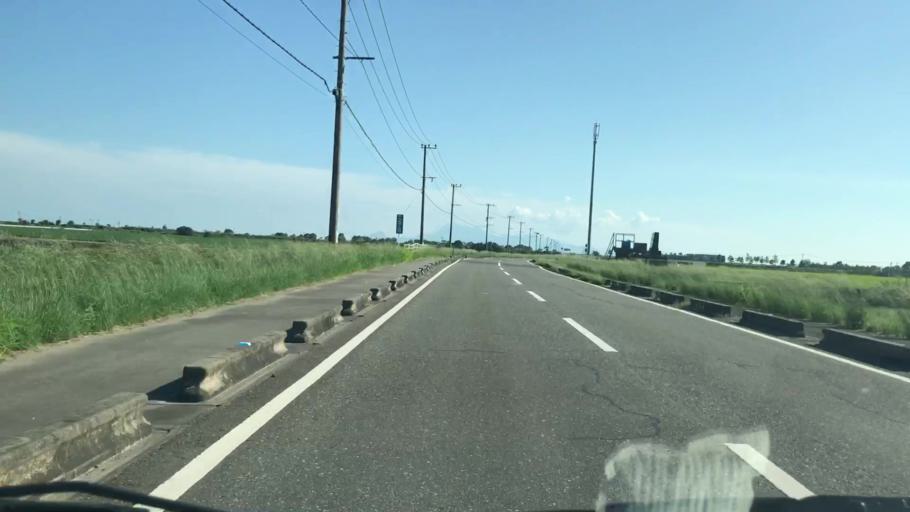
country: JP
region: Saga Prefecture
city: Okawa
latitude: 33.1596
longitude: 130.3086
